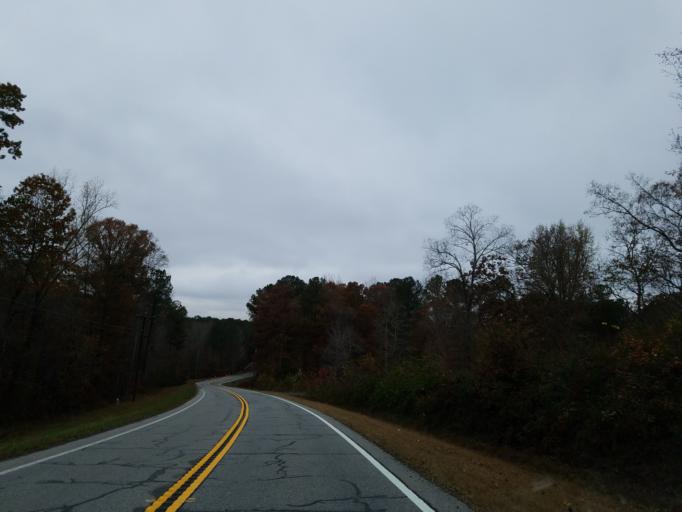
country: US
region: Georgia
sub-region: Cherokee County
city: Canton
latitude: 34.2291
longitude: -84.6176
